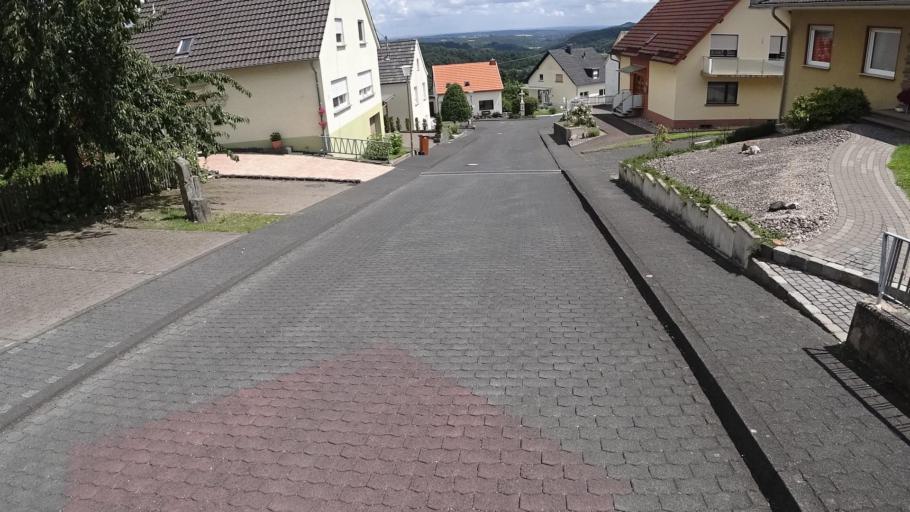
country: DE
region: Rheinland-Pfalz
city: Vettelschoss
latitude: 50.6185
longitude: 7.3469
